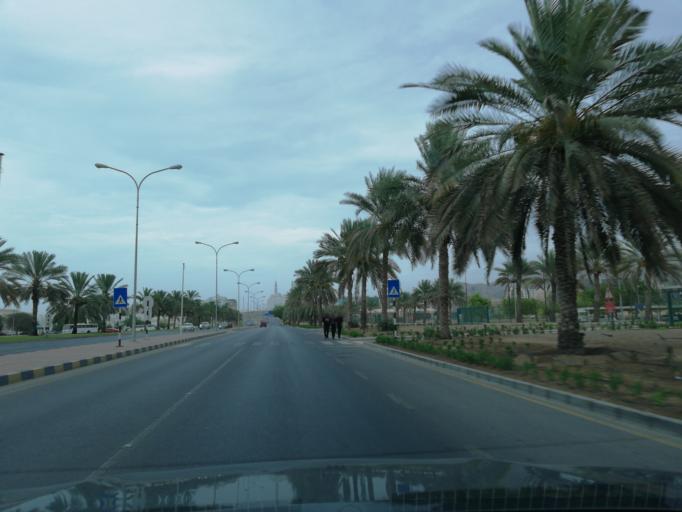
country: OM
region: Muhafazat Masqat
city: Bawshar
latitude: 23.5750
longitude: 58.4000
